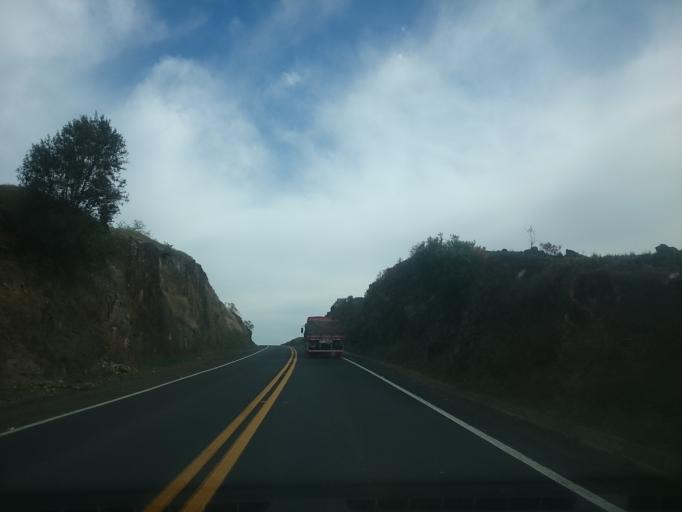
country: BR
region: Rio Grande do Sul
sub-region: Vacaria
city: Estrela
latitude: -28.1055
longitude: -50.6152
